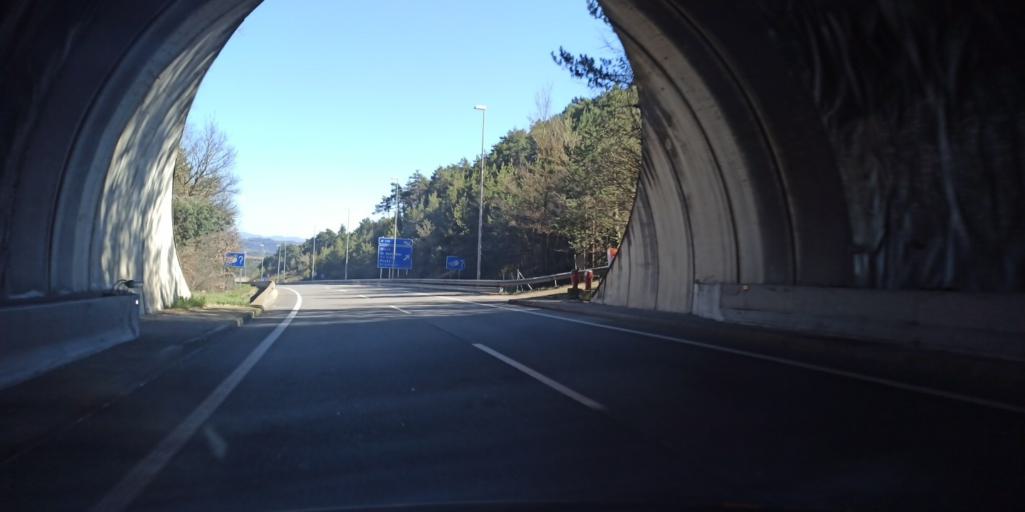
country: ES
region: Catalonia
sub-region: Provincia de Barcelona
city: Muntanyola
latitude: 41.9164
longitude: 2.1351
